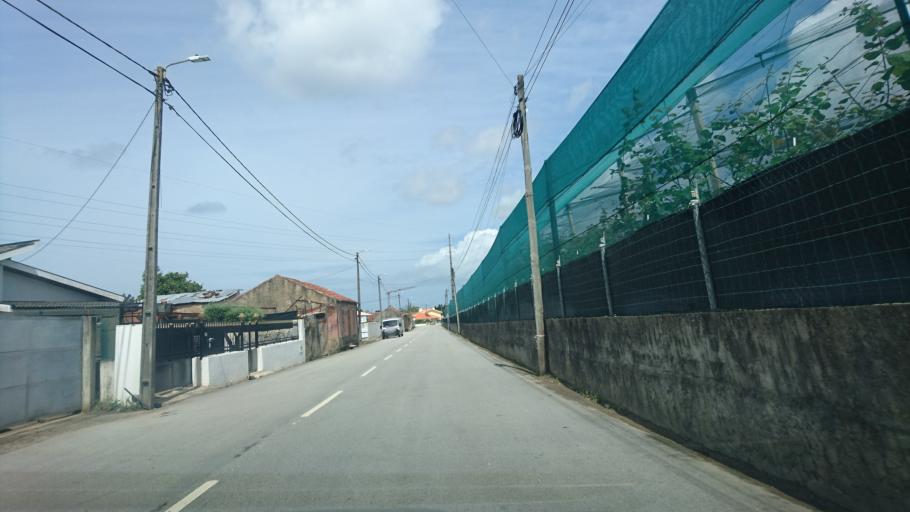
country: PT
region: Aveiro
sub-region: Santa Maria da Feira
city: Feira
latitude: 40.9163
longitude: -8.5794
